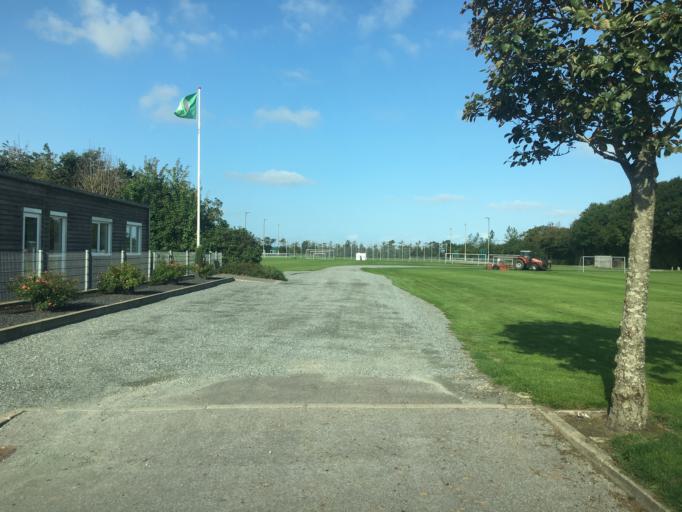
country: DK
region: South Denmark
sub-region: Tonder Kommune
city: Sherrebek
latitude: 55.1564
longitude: 8.7587
